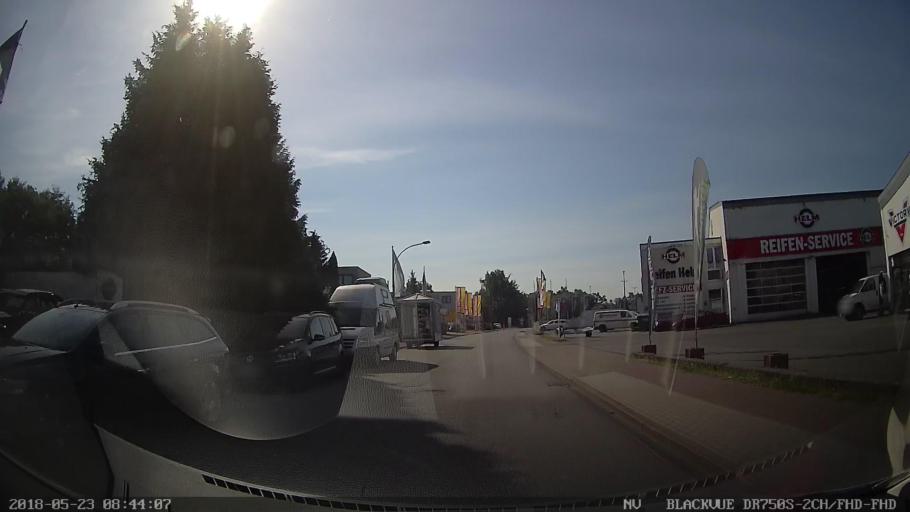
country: DE
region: Schleswig-Holstein
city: Pinneberg
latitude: 53.6740
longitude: 9.8012
